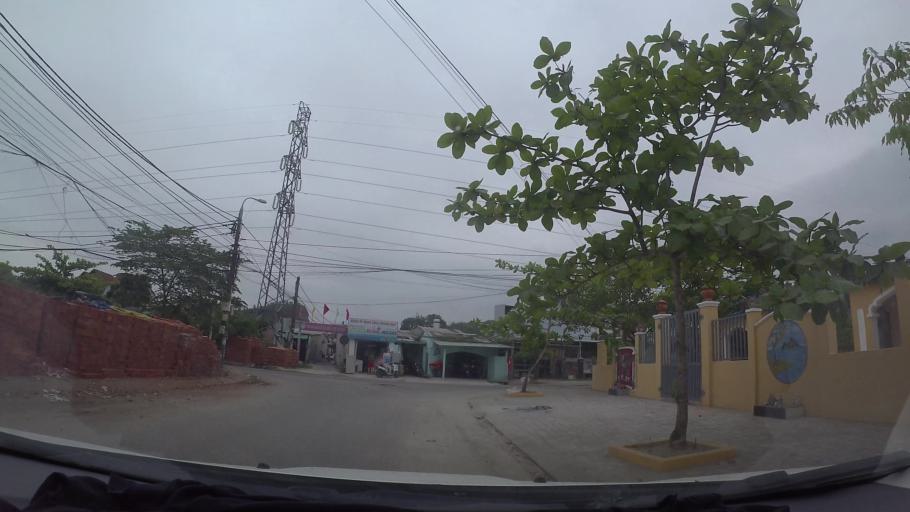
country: VN
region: Da Nang
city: Lien Chieu
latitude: 16.0692
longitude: 108.1453
